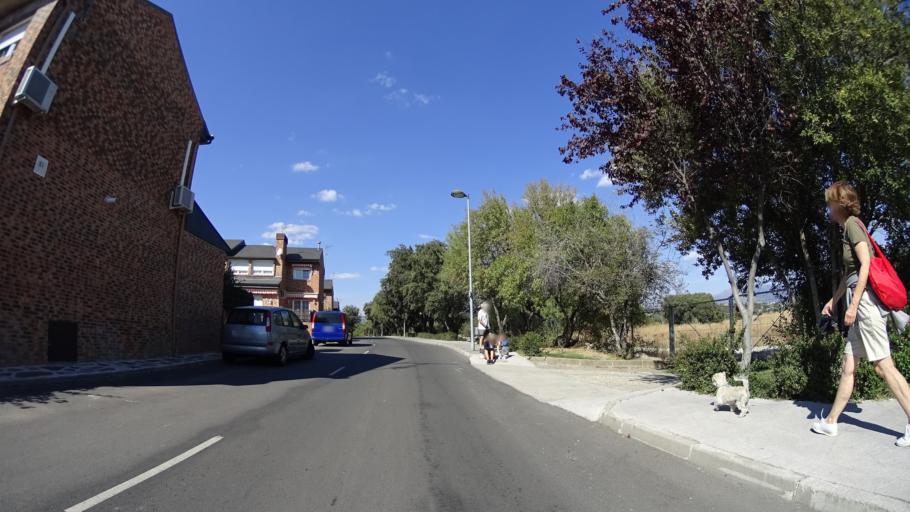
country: ES
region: Madrid
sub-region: Provincia de Madrid
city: Navalquejigo
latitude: 40.6094
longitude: -4.0291
